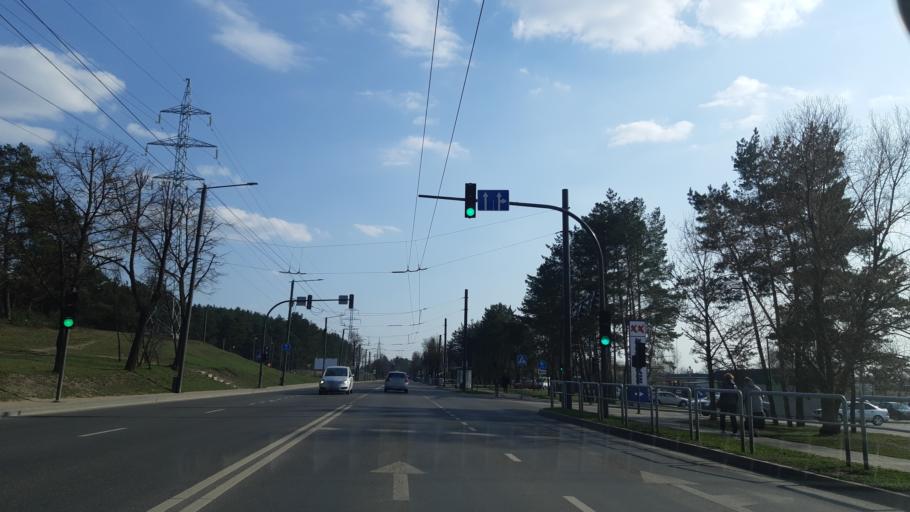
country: LT
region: Kauno apskritis
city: Dainava (Kaunas)
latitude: 54.8868
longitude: 24.0062
